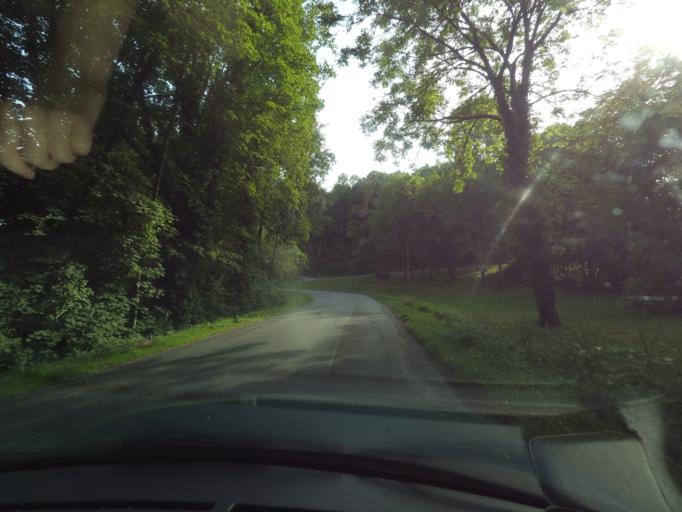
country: FR
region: Limousin
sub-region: Departement de la Haute-Vienne
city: Saint-Laurent-sur-Gorre
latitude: 45.7727
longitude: 0.9537
